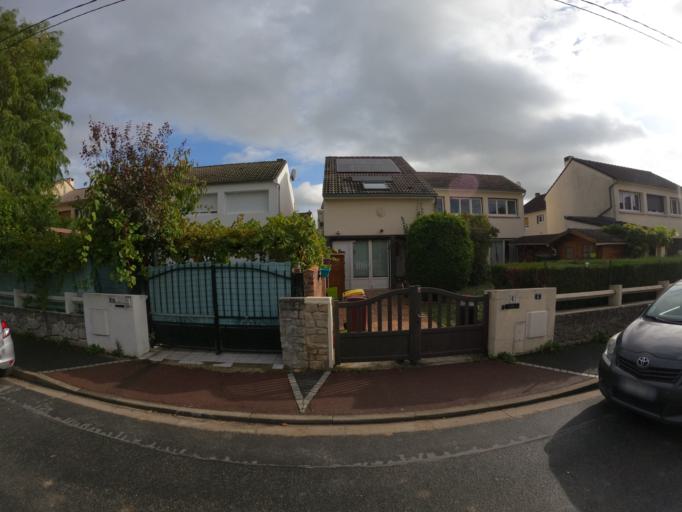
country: FR
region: Ile-de-France
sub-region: Departement de Seine-et-Marne
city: Courtry
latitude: 48.9105
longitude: 2.5989
